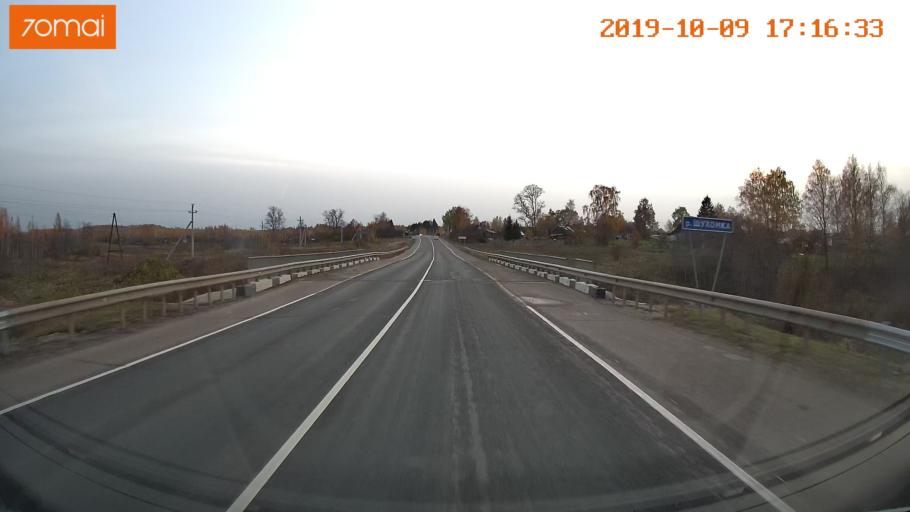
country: RU
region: Ivanovo
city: Furmanov
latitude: 57.2870
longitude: 41.1636
